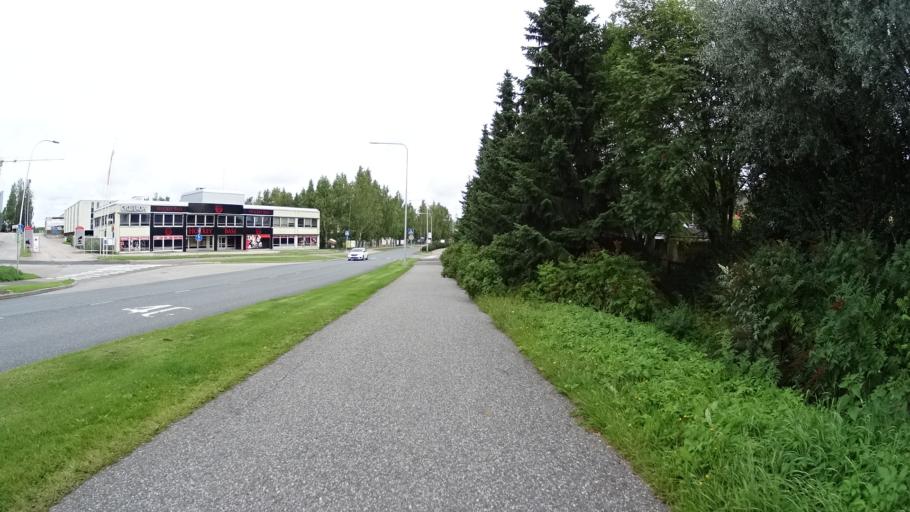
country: FI
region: Uusimaa
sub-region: Helsinki
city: Kilo
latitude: 60.2721
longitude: 24.8092
